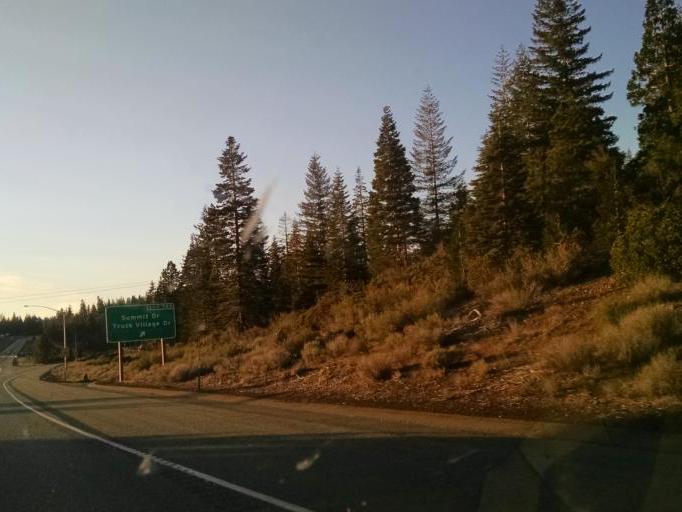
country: US
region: California
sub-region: Siskiyou County
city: Weed
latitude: 41.3650
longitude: -122.3668
